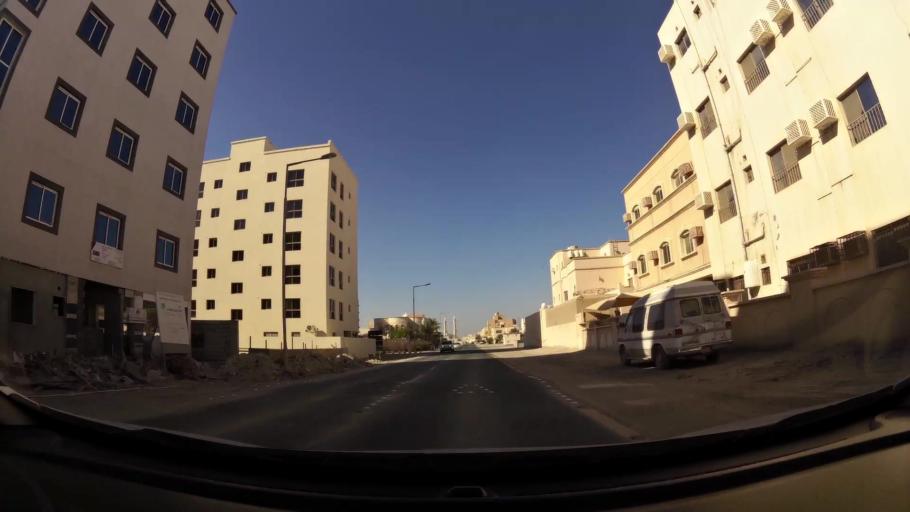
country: BH
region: Muharraq
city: Al Hadd
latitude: 26.2394
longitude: 50.6481
